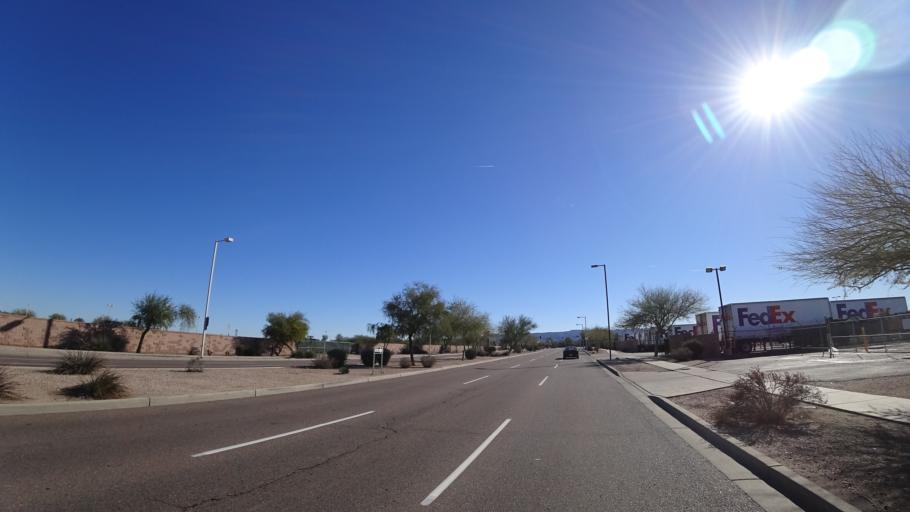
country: US
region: Arizona
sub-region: Maricopa County
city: Phoenix
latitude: 33.4336
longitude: -112.0348
